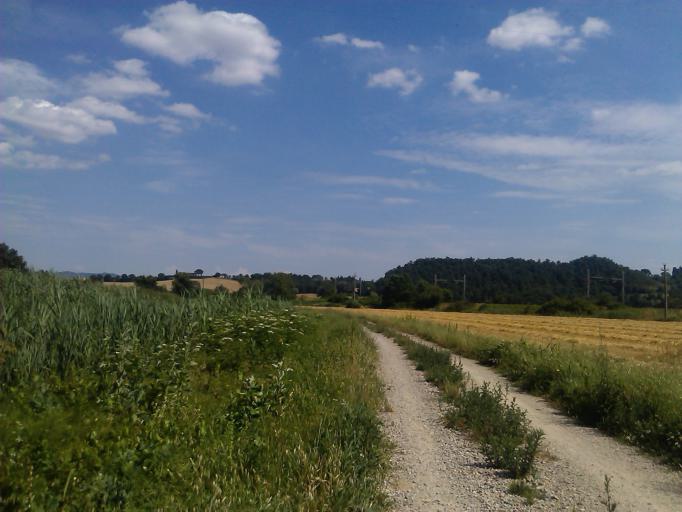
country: IT
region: Tuscany
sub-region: Provincia di Siena
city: Chiusi
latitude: 43.0536
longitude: 11.9388
